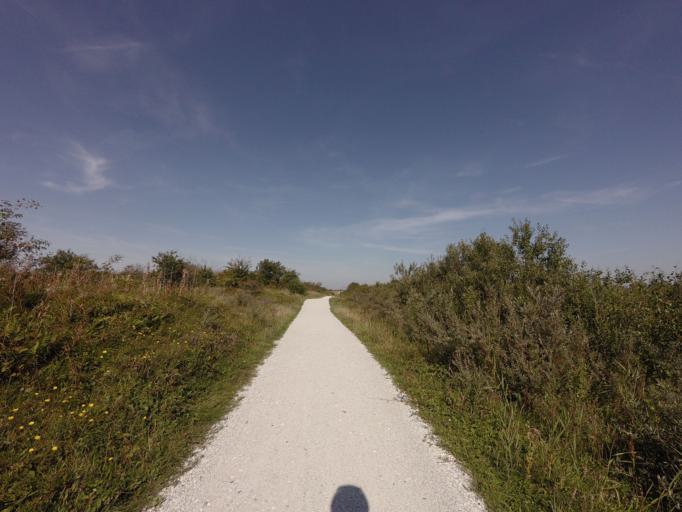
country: NL
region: Friesland
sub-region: Gemeente Schiermonnikoog
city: Schiermonnikoog
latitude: 53.4723
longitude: 6.1444
